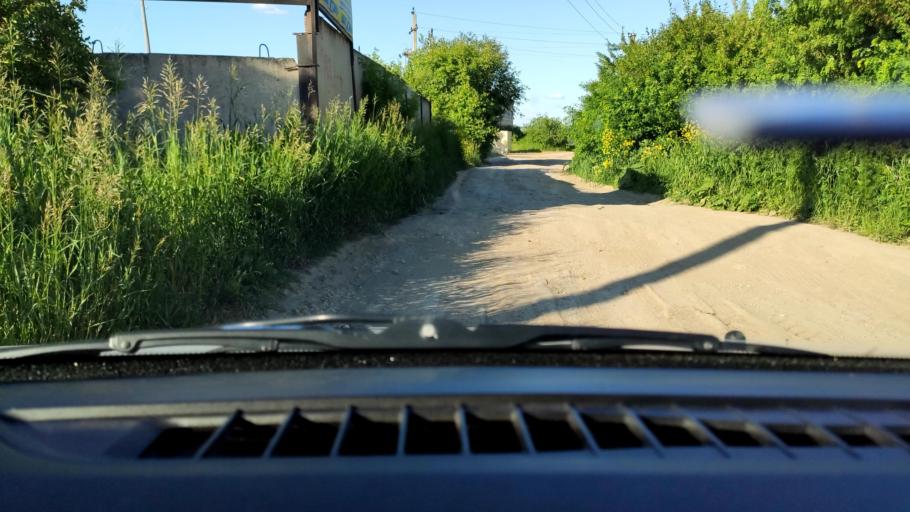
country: RU
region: Perm
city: Orda
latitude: 57.1877
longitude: 56.9164
